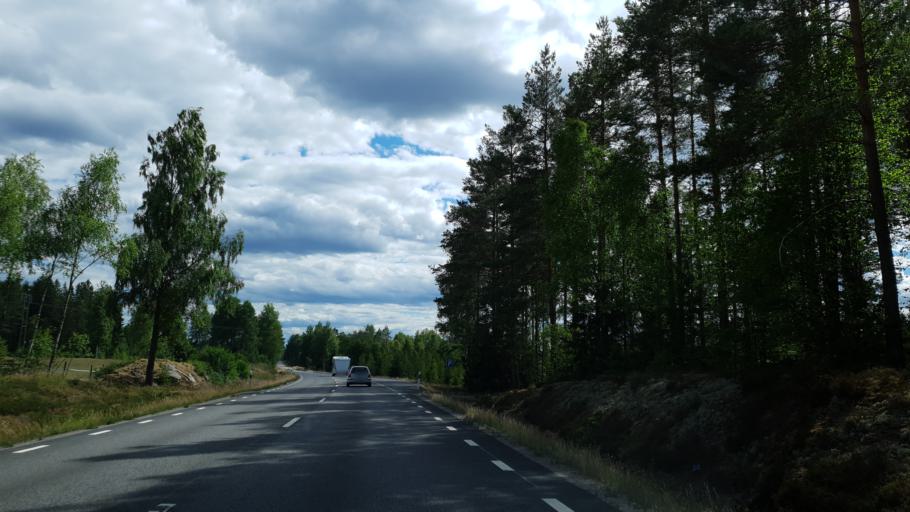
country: SE
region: Kronoberg
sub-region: Lessebo Kommun
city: Lessebo
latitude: 56.7985
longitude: 15.4120
